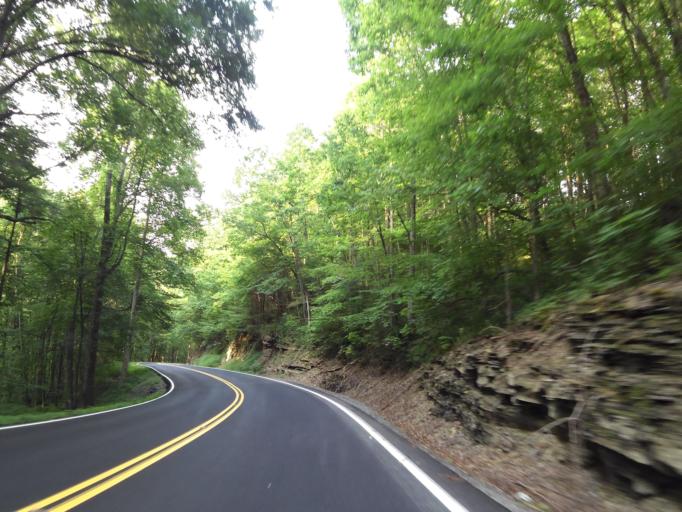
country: US
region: Tennessee
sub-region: Morgan County
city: Coalfield
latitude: 36.1208
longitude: -84.4342
